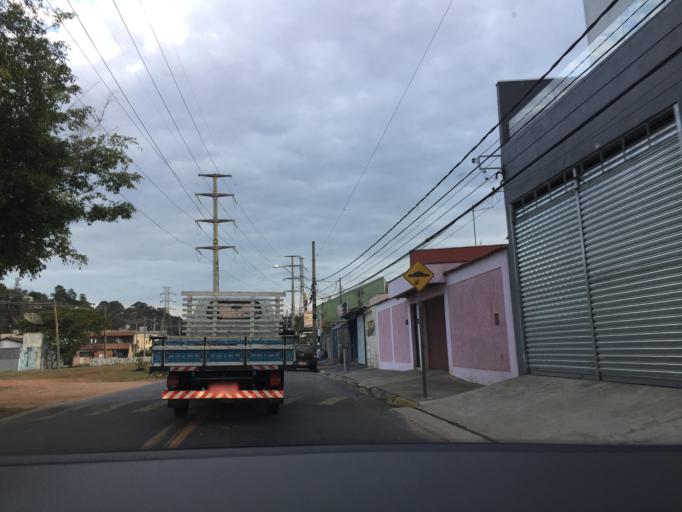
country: BR
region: Sao Paulo
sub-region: Varzea Paulista
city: Varzea Paulista
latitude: -23.2106
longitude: -46.8395
